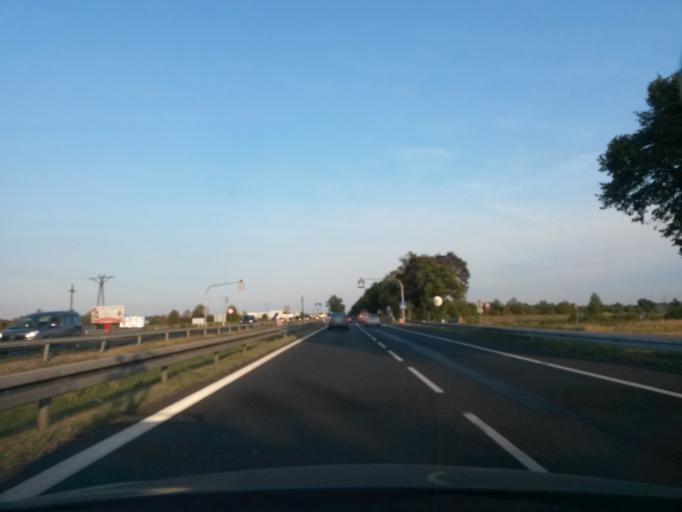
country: PL
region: Masovian Voivodeship
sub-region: Powiat nowodworski
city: Nowy Dwor Mazowiecki
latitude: 52.3843
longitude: 20.7518
